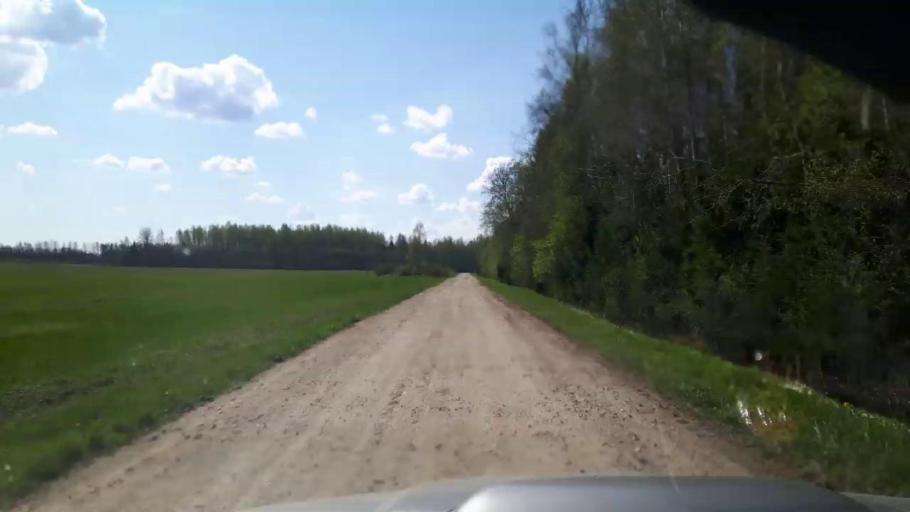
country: EE
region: Paernumaa
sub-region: Tootsi vald
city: Tootsi
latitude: 58.4938
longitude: 24.9429
